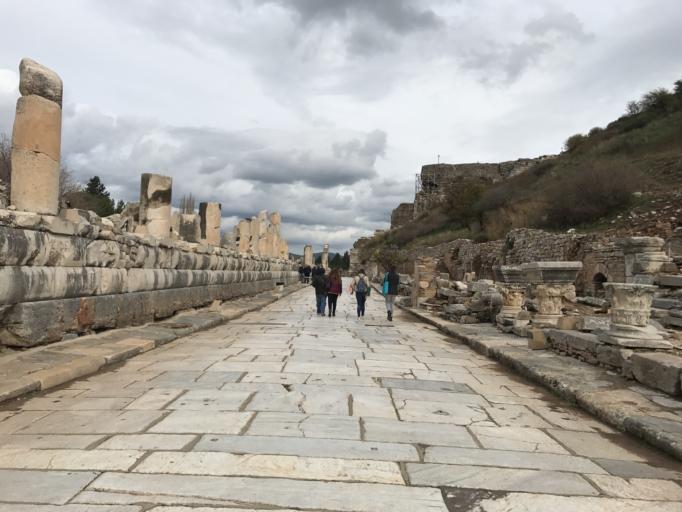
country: TR
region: Izmir
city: Selcuk
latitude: 37.9393
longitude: 27.3415
